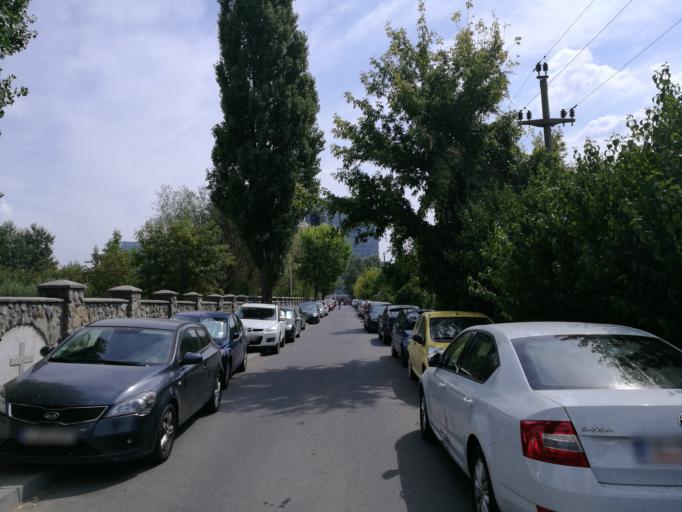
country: RO
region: Bucuresti
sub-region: Municipiul Bucuresti
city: Bucharest
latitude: 44.4841
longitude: 26.1032
